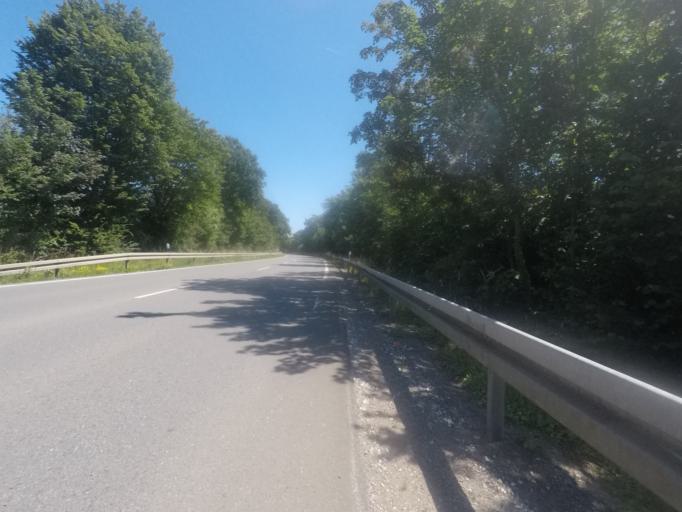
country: DE
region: North Rhine-Westphalia
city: Enger
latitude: 52.0987
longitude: 8.5671
